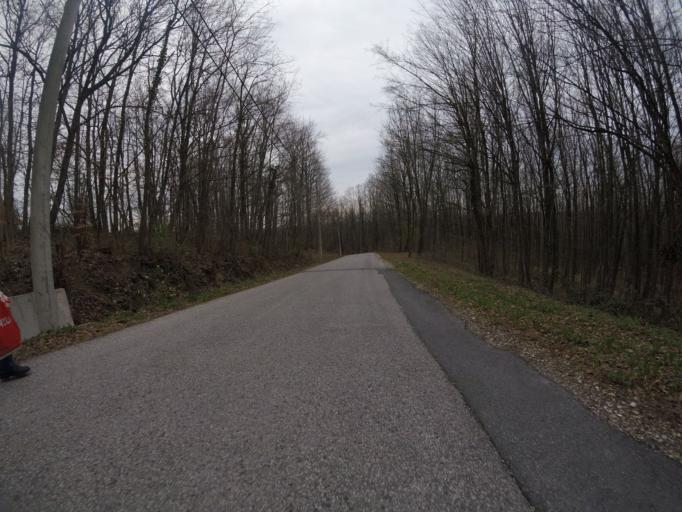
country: HR
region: Grad Zagreb
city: Strmec
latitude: 45.6335
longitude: 15.9360
